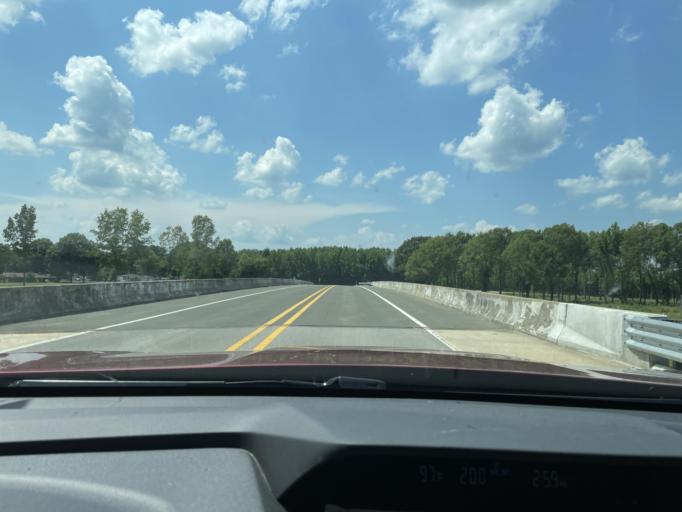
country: US
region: Arkansas
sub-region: Woodruff County
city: Augusta
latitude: 35.4194
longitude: -91.4446
